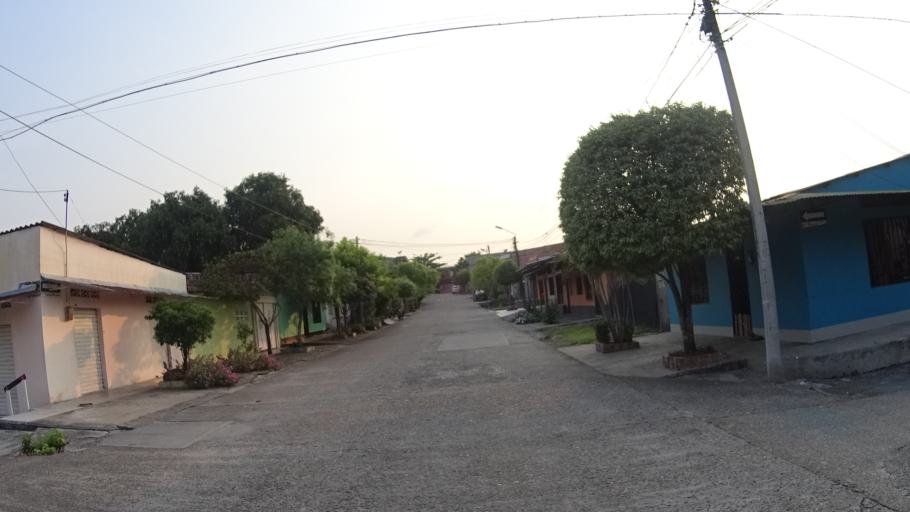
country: CO
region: Caldas
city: La Dorada
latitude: 5.4506
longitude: -74.6705
